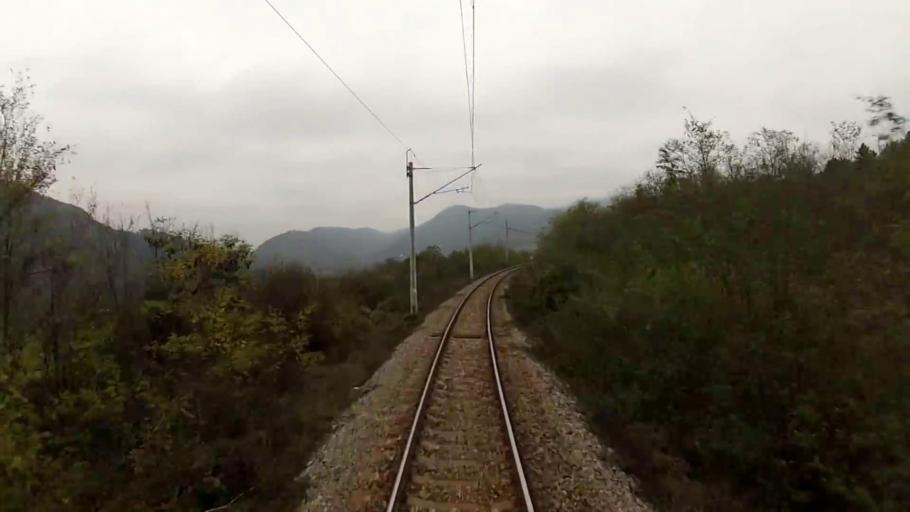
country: RS
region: Central Serbia
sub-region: Pirotski Okrug
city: Dimitrovgrad
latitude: 42.9875
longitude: 22.8515
